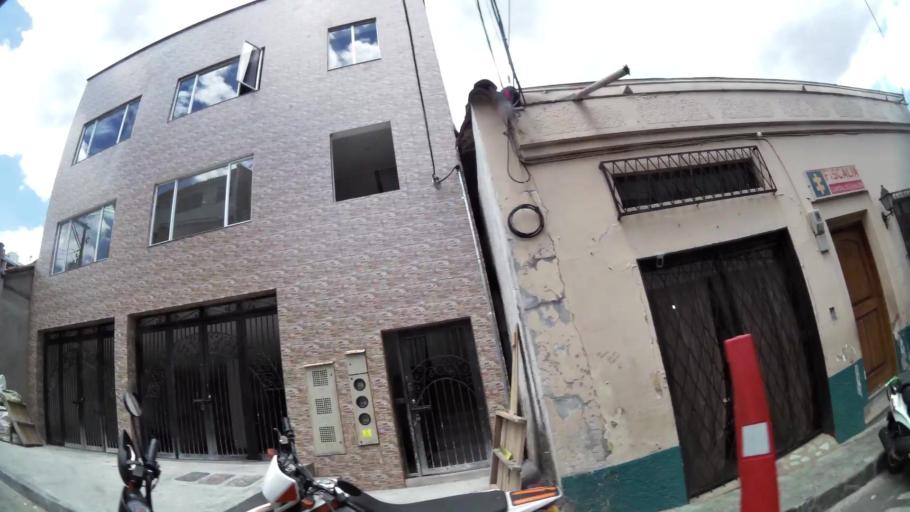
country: CO
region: Antioquia
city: La Estrella
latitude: 6.1584
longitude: -75.6442
